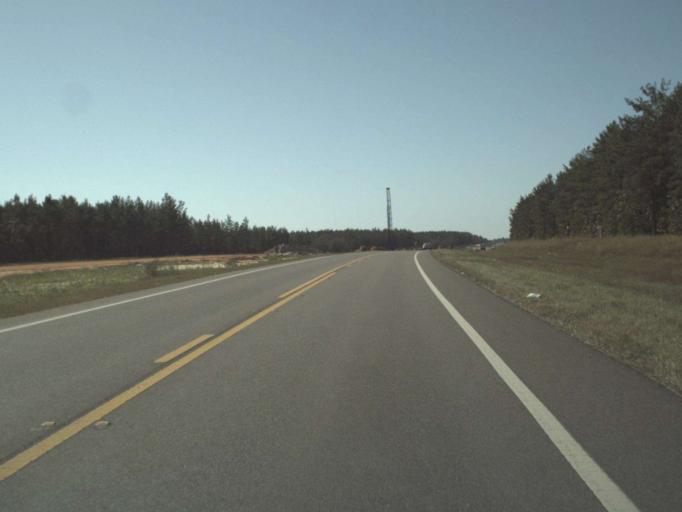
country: US
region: Florida
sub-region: Walton County
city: Freeport
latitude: 30.5195
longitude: -86.1092
